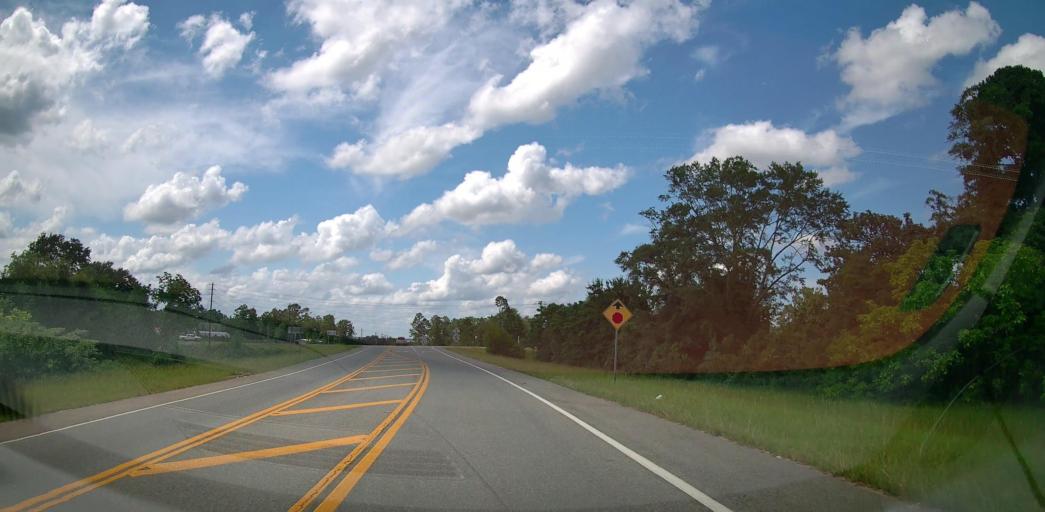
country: US
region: Georgia
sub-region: Houston County
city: Centerville
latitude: 32.6726
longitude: -83.7089
